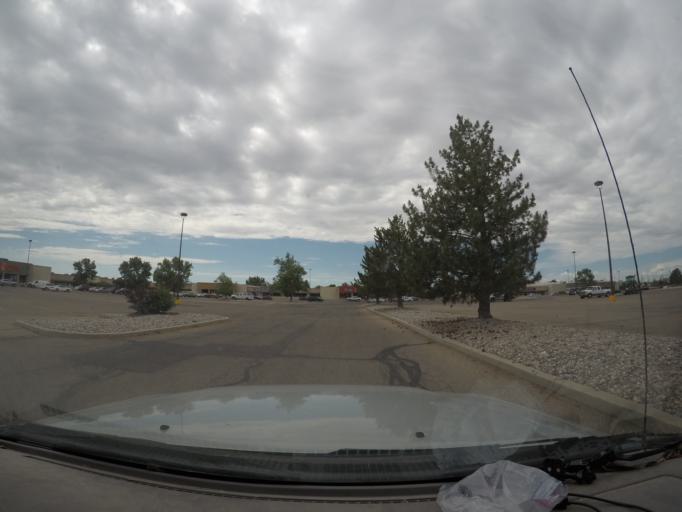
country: US
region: Wyoming
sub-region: Laramie County
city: Fox Farm-College
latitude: 41.1386
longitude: -104.7652
